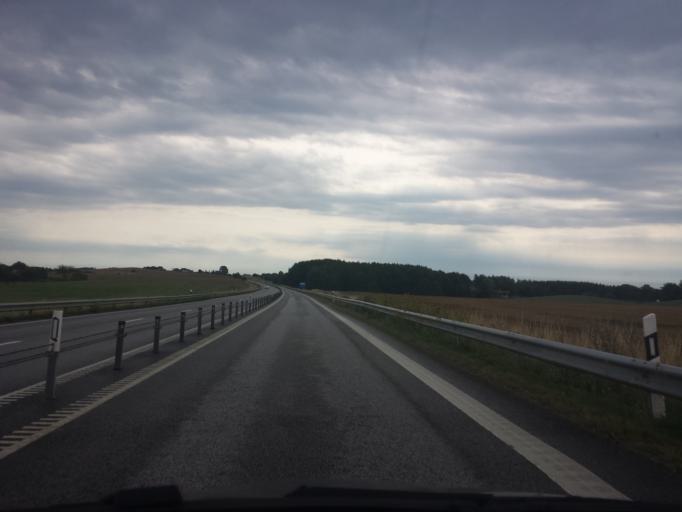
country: SE
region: Skane
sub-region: Ystads Kommun
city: Ystad
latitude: 55.4612
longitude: 13.7257
